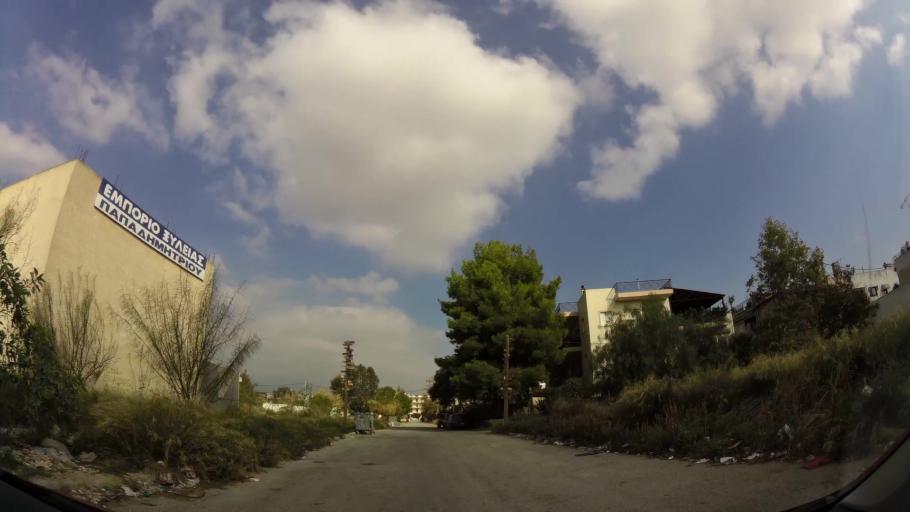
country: GR
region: Attica
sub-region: Nomarchia Dytikis Attikis
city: Zefyri
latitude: 38.0549
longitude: 23.7317
